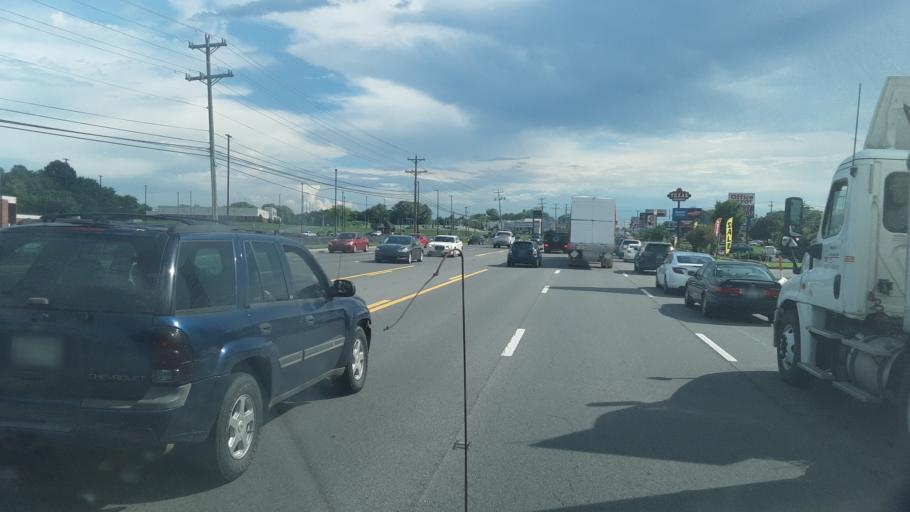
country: US
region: Tennessee
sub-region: Montgomery County
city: Clarksville
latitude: 36.5846
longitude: -87.2958
